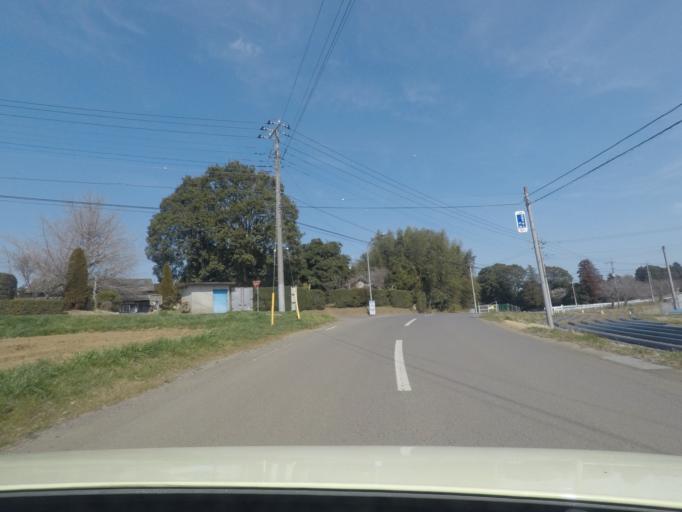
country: JP
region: Ibaraki
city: Okunoya
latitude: 36.1978
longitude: 140.4018
